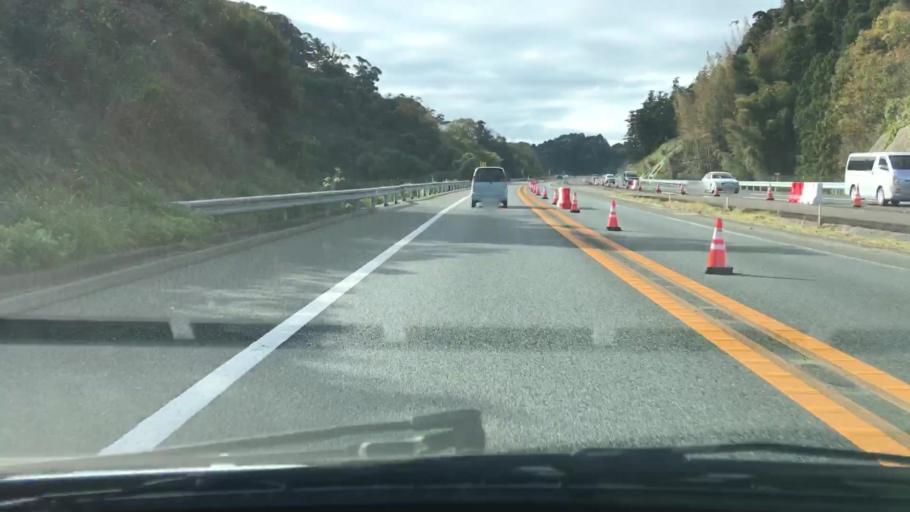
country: JP
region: Chiba
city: Kimitsu
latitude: 35.2764
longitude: 139.9220
